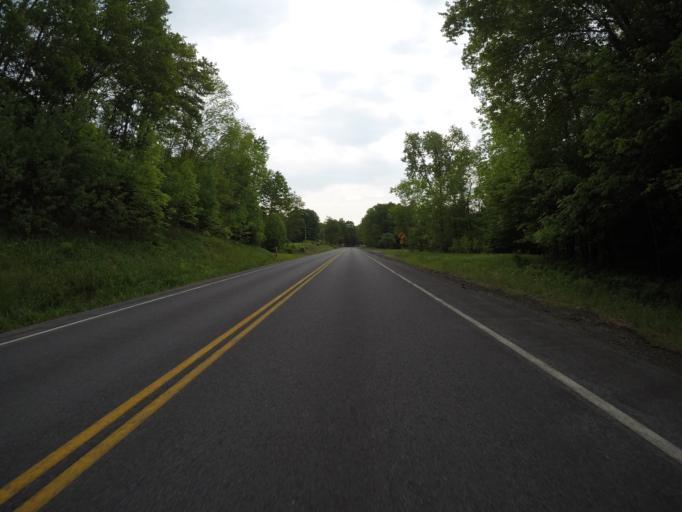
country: US
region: New York
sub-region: Sullivan County
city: Livingston Manor
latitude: 42.0648
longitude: -74.9396
